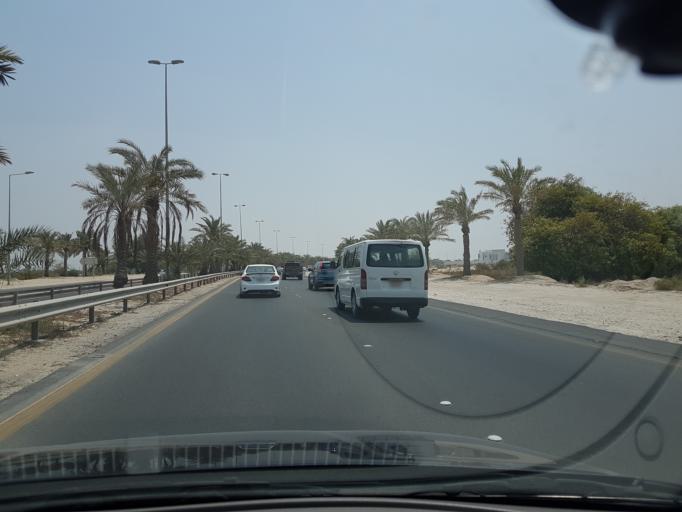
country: BH
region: Northern
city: Ar Rifa'
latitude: 26.1477
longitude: 50.5389
